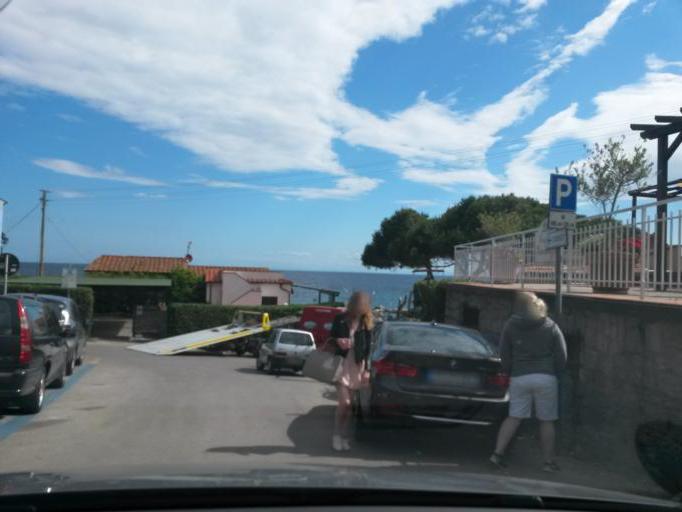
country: IT
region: Tuscany
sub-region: Provincia di Livorno
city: Marciana
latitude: 42.8066
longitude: 10.1409
